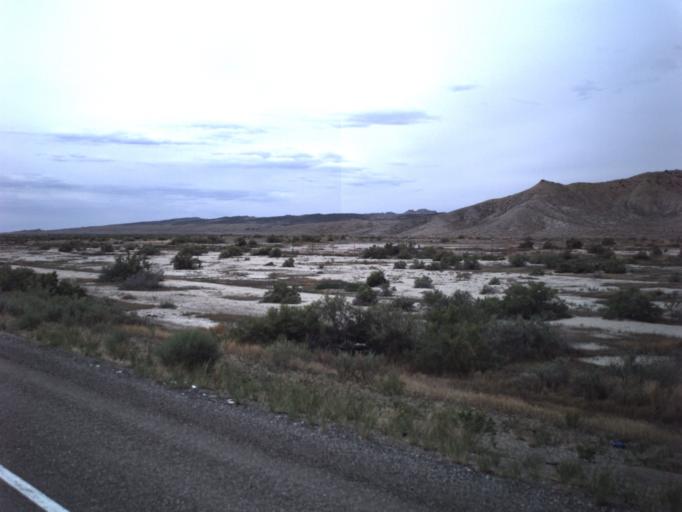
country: US
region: Utah
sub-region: Carbon County
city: East Carbon City
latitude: 39.2425
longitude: -110.3389
